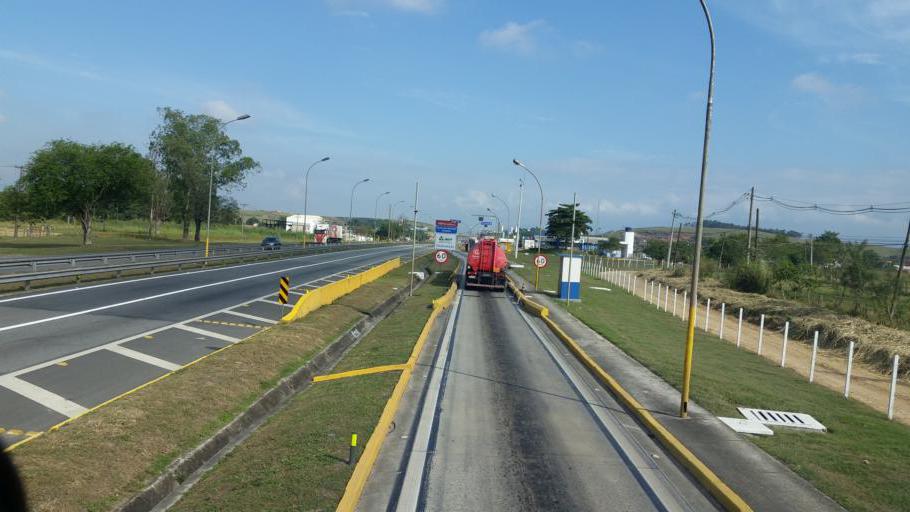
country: BR
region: Rio de Janeiro
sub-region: Resende
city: Resende
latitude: -22.4566
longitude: -44.4082
